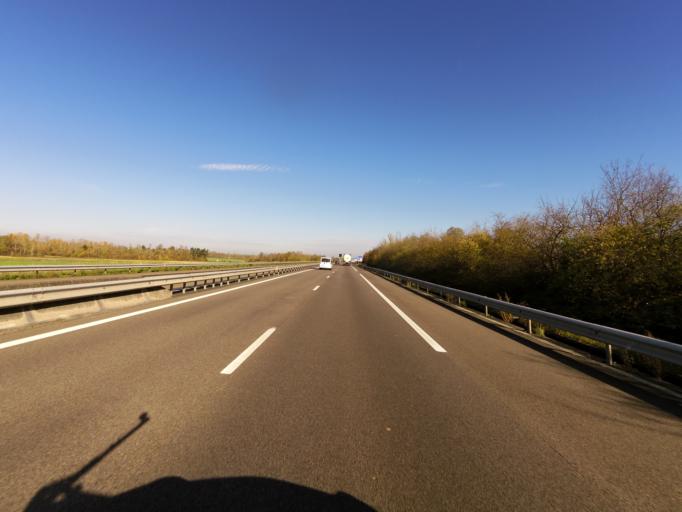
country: FR
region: Champagne-Ardenne
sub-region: Departement de la Marne
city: Fagnieres
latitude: 48.9975
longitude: 4.2971
